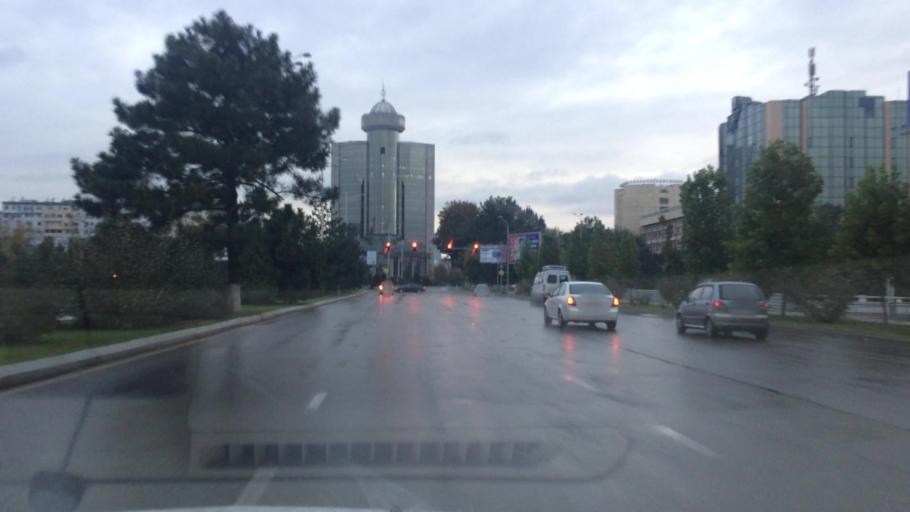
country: UZ
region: Toshkent Shahri
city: Tashkent
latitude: 41.3119
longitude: 69.2423
